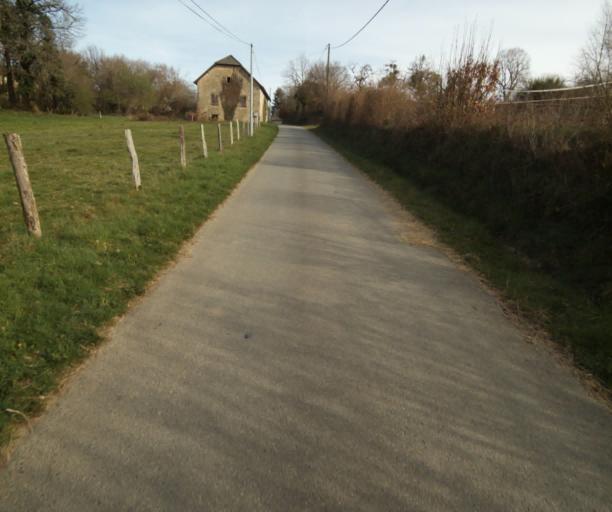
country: FR
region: Limousin
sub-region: Departement de la Correze
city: Chamboulive
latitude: 45.4446
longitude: 1.7536
